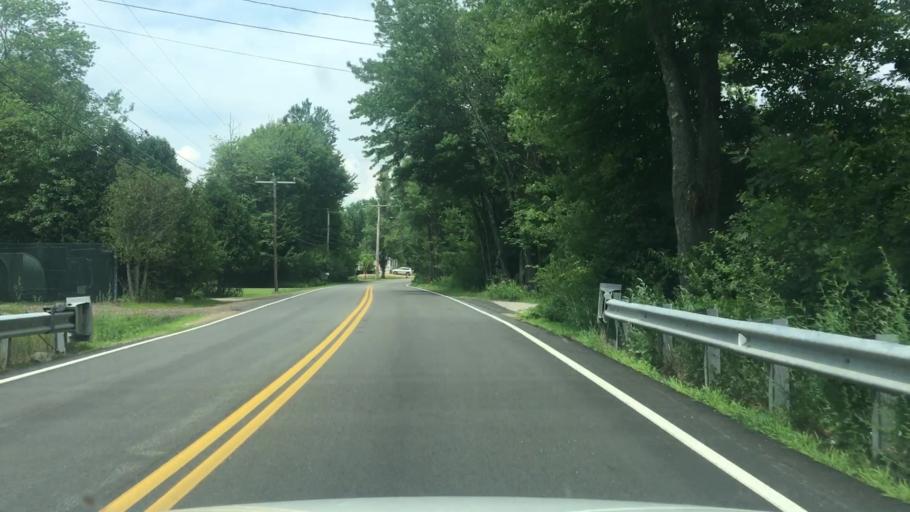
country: US
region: New Hampshire
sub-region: Strafford County
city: Rochester
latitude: 43.3356
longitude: -70.9582
